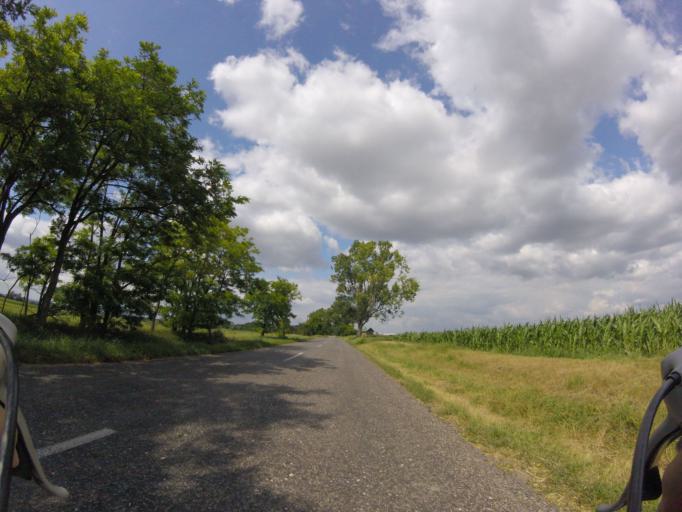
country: HU
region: Fejer
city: Seregelyes
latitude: 47.1350
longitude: 18.5761
